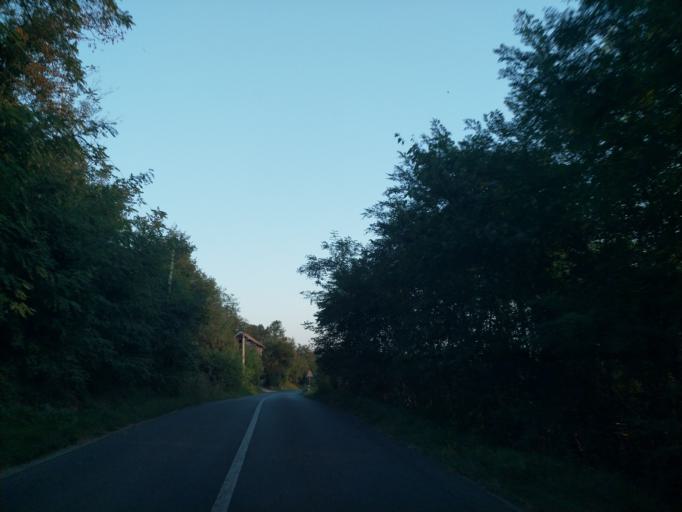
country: RS
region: Central Serbia
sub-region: Rasinski Okrug
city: Krusevac
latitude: 43.6117
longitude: 21.2086
